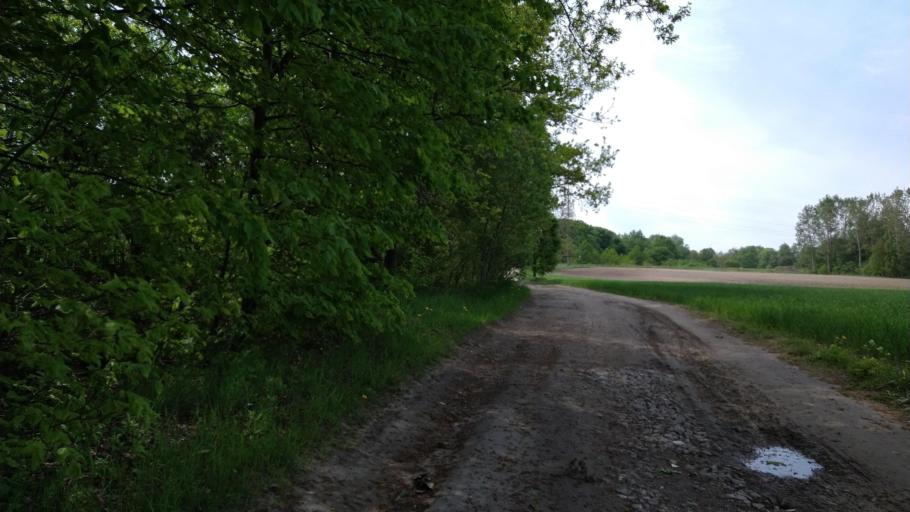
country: PL
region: Warmian-Masurian Voivodeship
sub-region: Powiat olsztynski
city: Olsztyn
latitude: 53.7932
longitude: 20.5476
